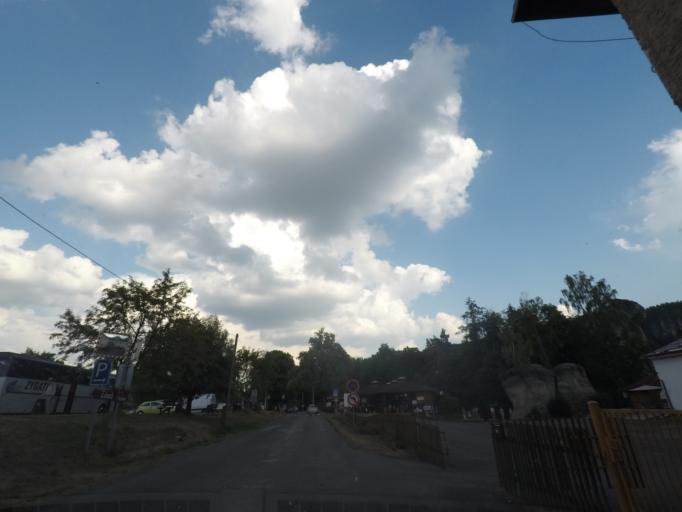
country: CZ
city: Teplice nad Metuji
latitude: 50.6168
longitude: 16.1220
